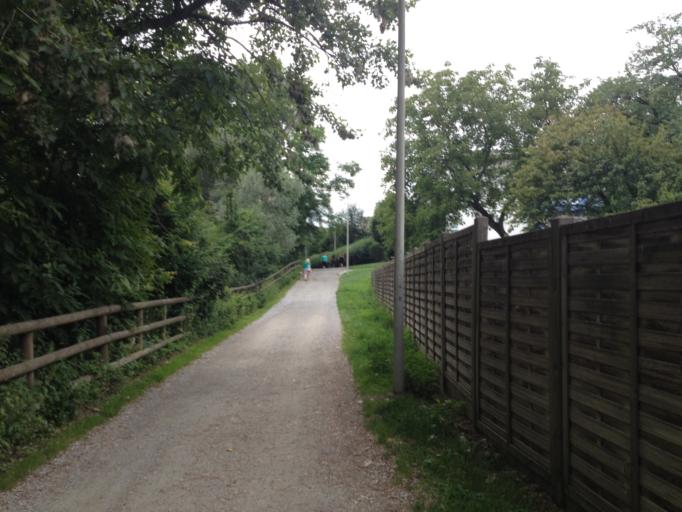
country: AT
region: Styria
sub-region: Graz Stadt
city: Goesting
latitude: 47.0968
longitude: 15.4162
